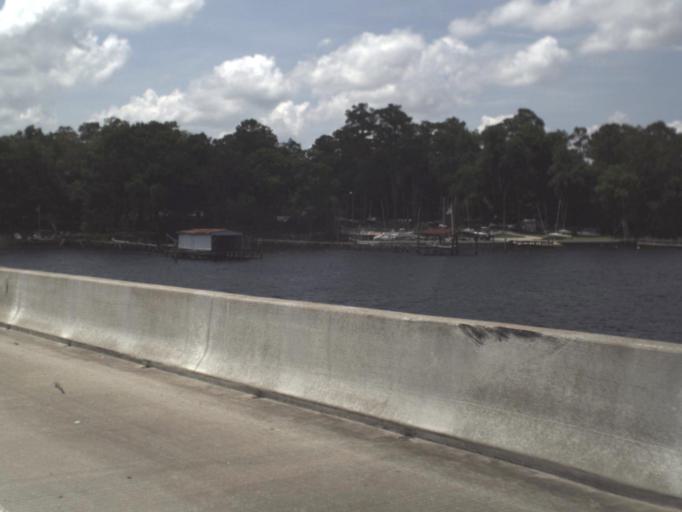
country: US
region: Florida
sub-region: Clay County
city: Orange Park
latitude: 30.1914
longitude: -81.6891
